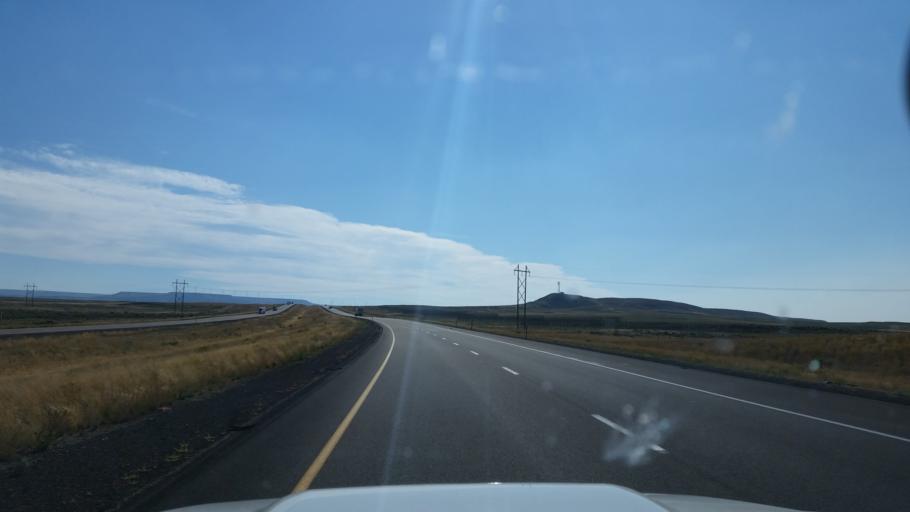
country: US
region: Wyoming
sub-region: Uinta County
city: Lyman
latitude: 41.3537
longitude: -110.3727
